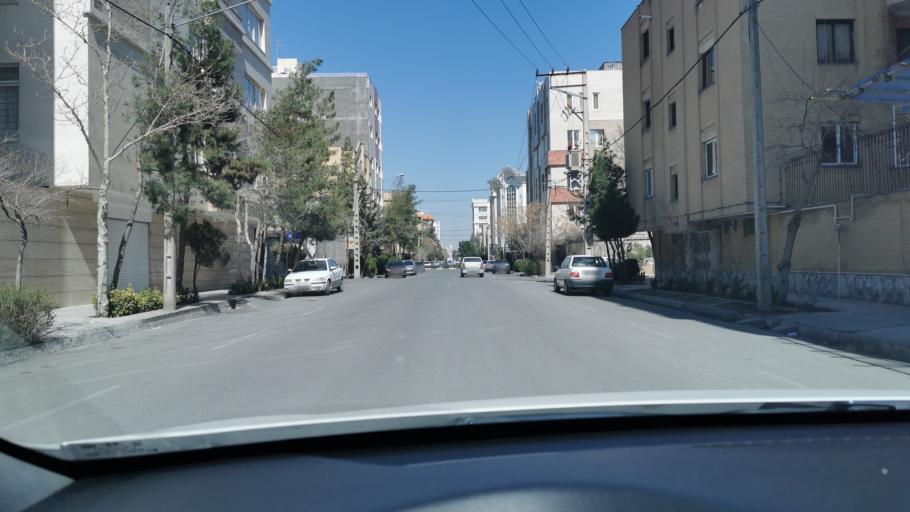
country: IR
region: Razavi Khorasan
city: Mashhad
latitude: 36.3265
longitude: 59.5162
